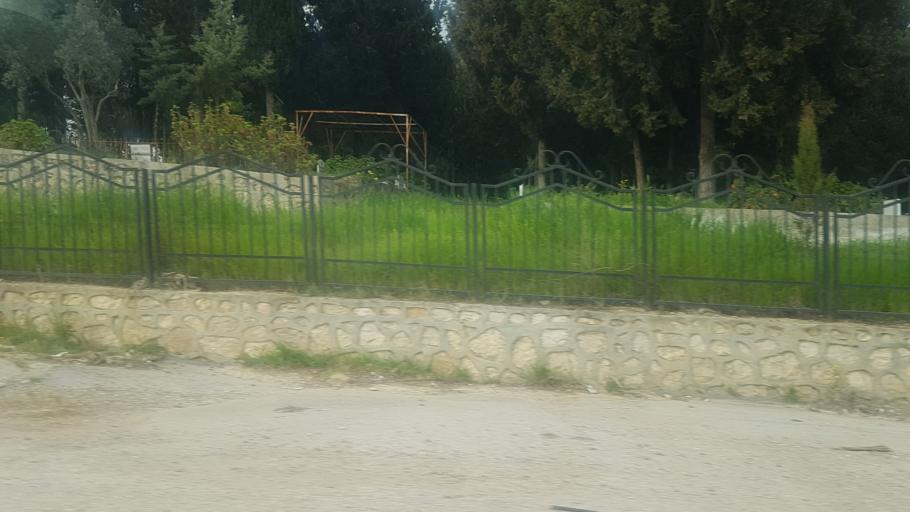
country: TR
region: Adana
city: Seyhan
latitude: 37.0509
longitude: 35.2070
